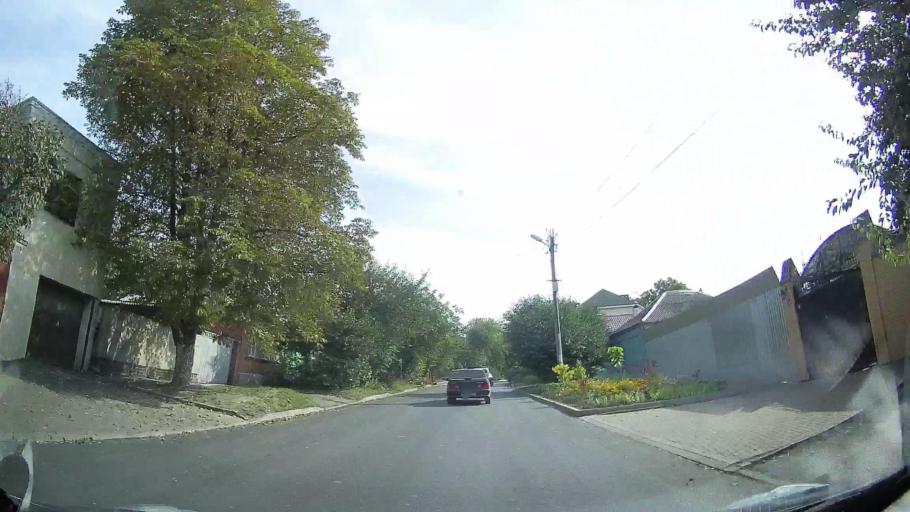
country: RU
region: Rostov
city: Severnyy
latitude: 47.2642
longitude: 39.7086
